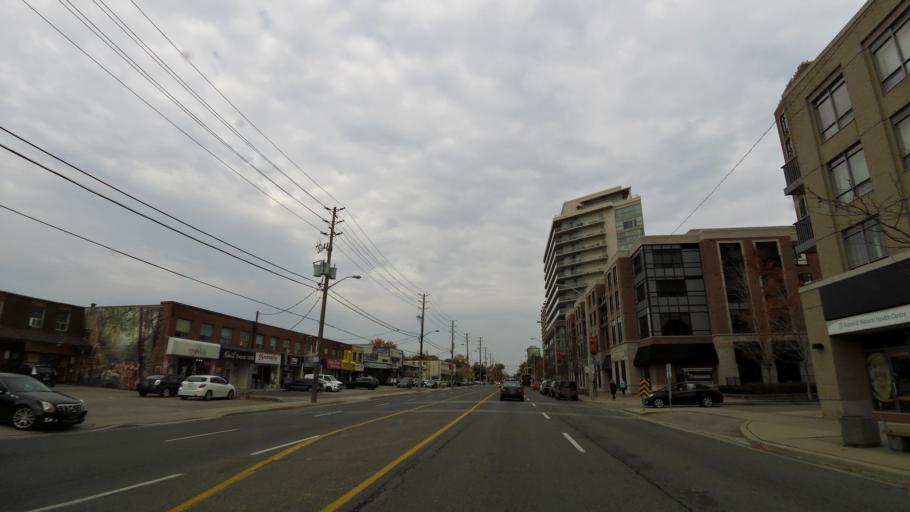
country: CA
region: Ontario
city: Etobicoke
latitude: 43.6439
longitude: -79.5331
